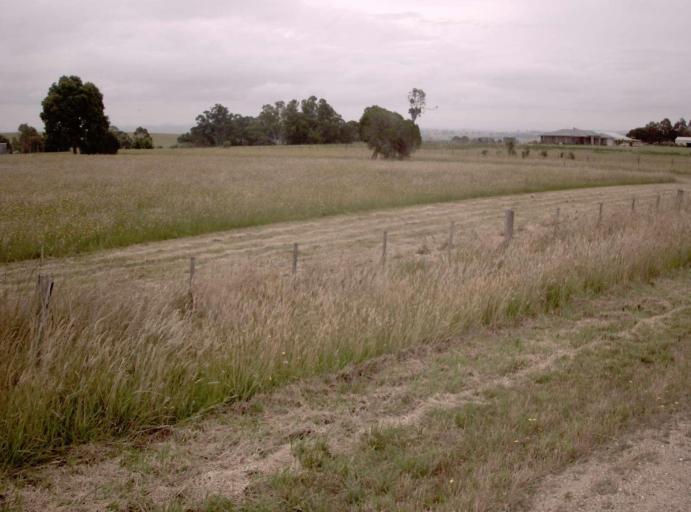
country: AU
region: Victoria
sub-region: East Gippsland
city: Bairnsdale
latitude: -37.8073
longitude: 147.4382
